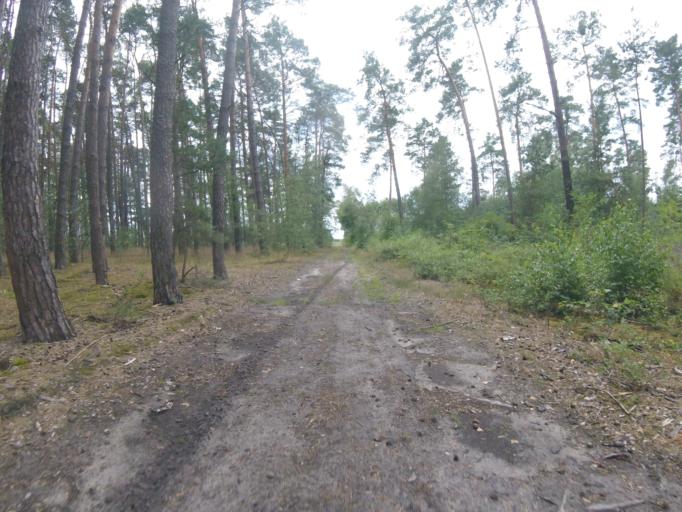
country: DE
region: Brandenburg
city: Bestensee
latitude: 52.2659
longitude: 13.7144
